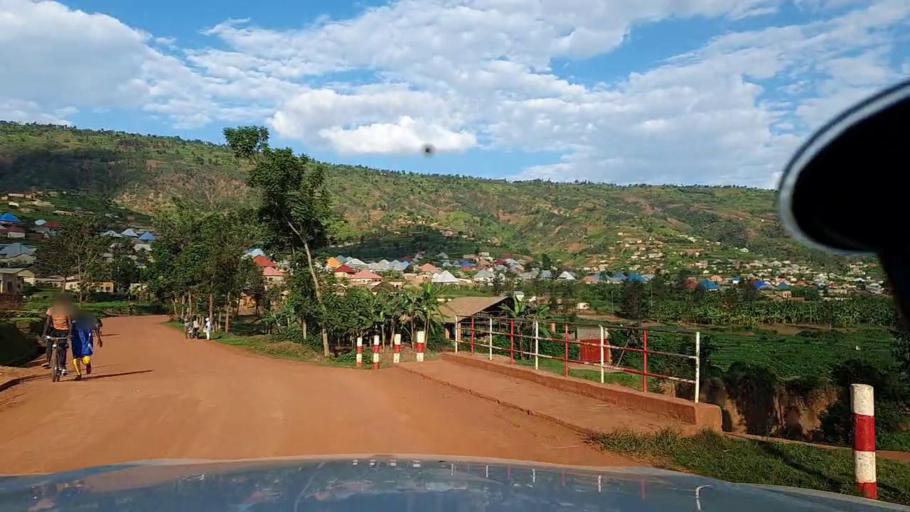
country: RW
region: Kigali
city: Kigali
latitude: -1.9026
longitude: 29.9727
